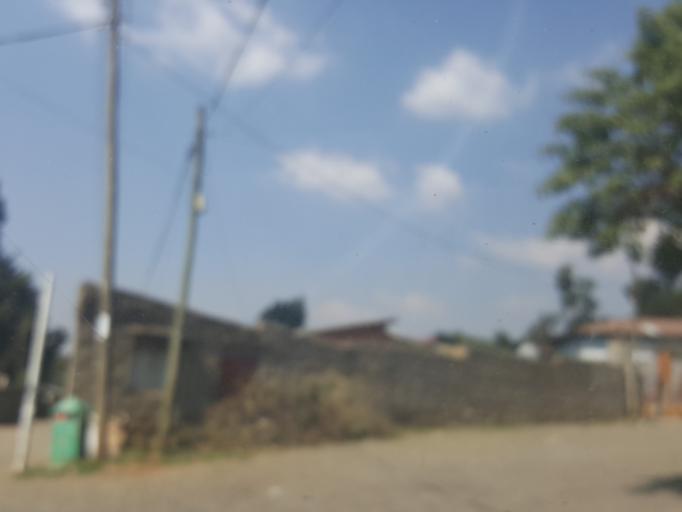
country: ET
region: Adis Abeba
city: Addis Ababa
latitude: 9.0530
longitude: 38.7336
